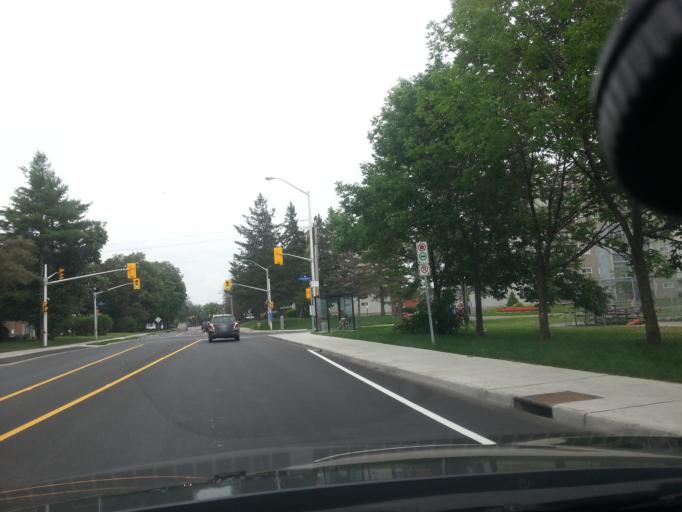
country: CA
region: Ontario
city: Ottawa
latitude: 45.3595
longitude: -75.7226
